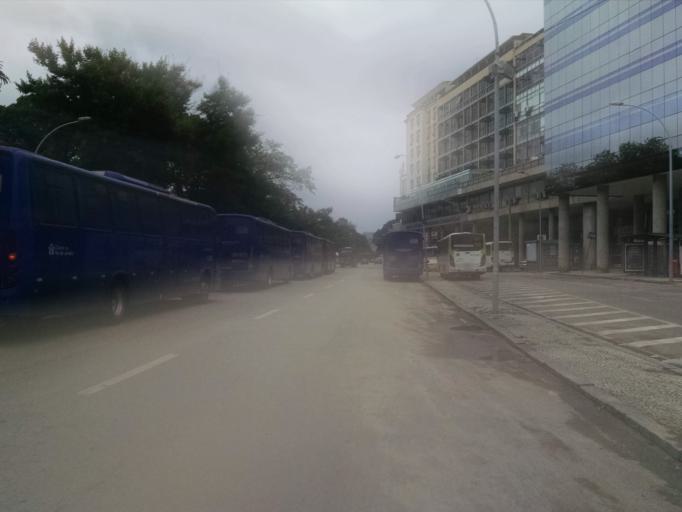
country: BR
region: Rio de Janeiro
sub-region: Rio De Janeiro
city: Rio de Janeiro
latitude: -22.9070
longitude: -43.1686
